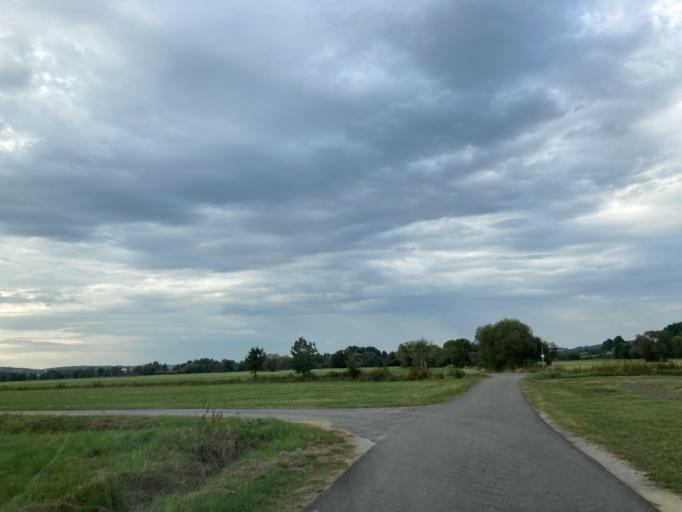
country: DE
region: Baden-Wuerttemberg
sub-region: Freiburg Region
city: Donaueschingen
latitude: 47.9430
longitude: 8.5408
